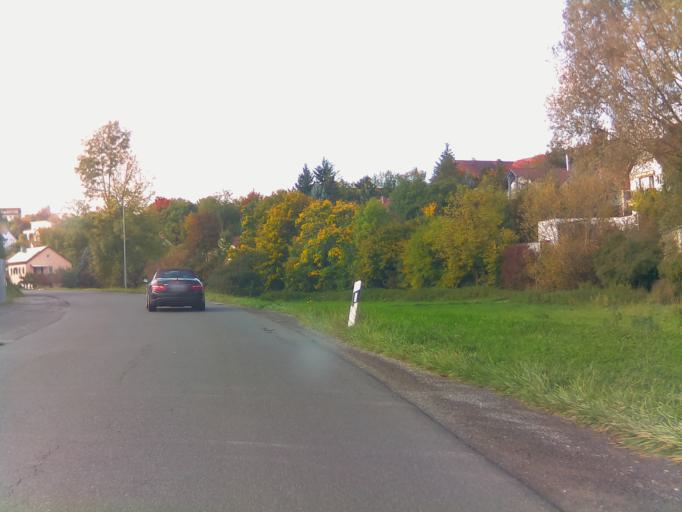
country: DE
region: Bavaria
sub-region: Regierungsbezirk Unterfranken
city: Kitzingen
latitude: 49.7379
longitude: 10.1445
